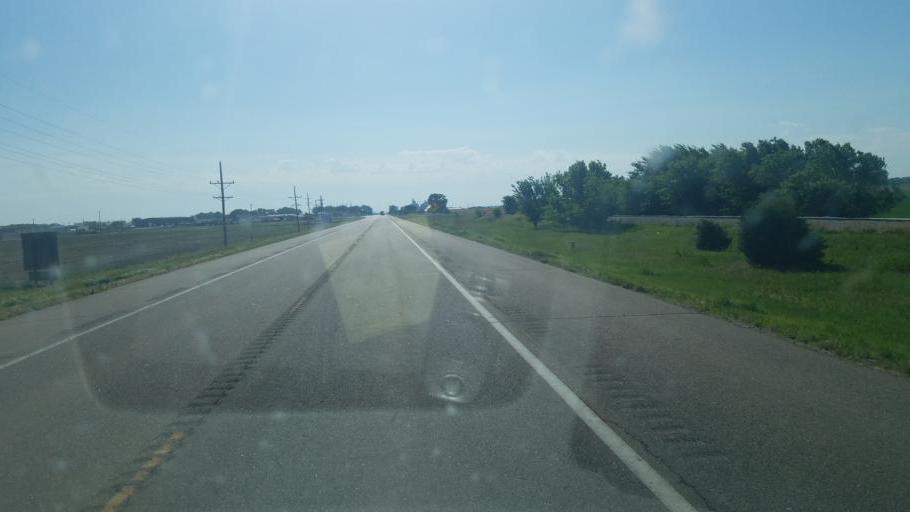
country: US
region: Kansas
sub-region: Barton County
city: Great Bend
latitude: 38.3651
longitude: -98.7045
